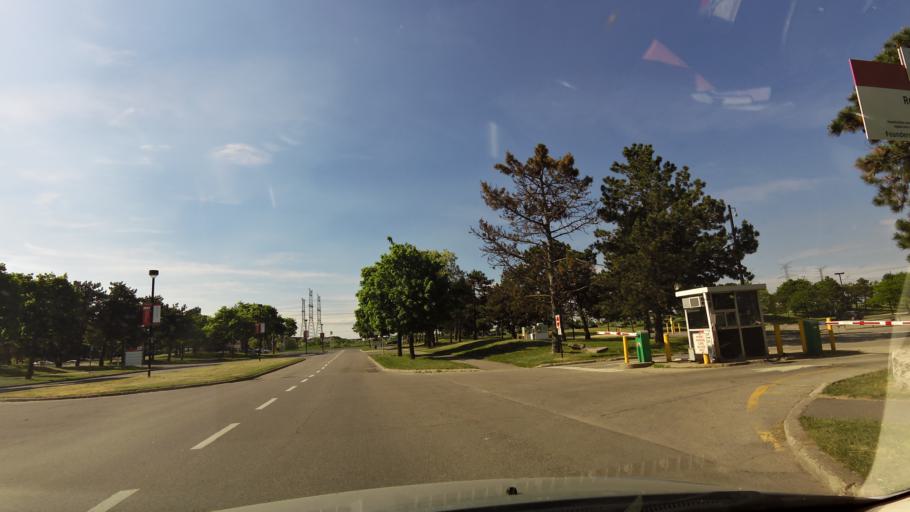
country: CA
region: Ontario
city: Concord
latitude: 43.7780
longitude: -79.5037
